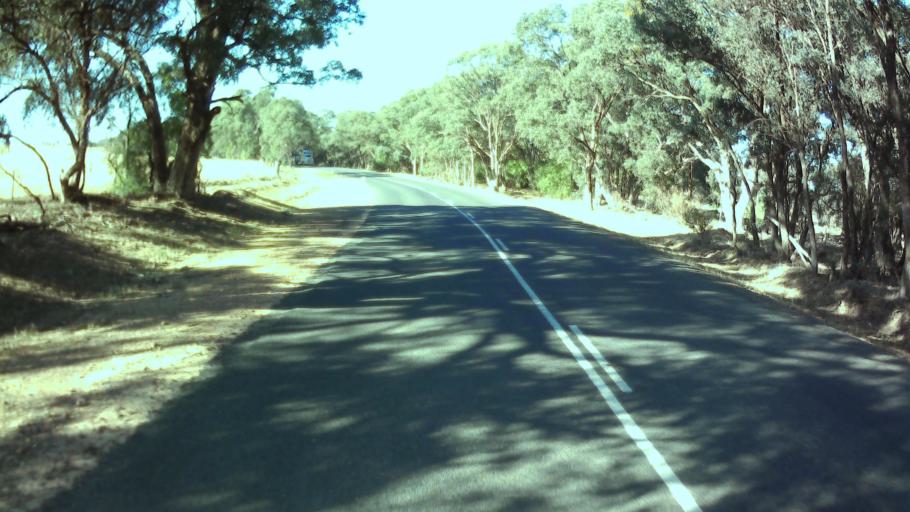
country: AU
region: New South Wales
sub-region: Weddin
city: Grenfell
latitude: -33.9933
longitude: 148.1338
